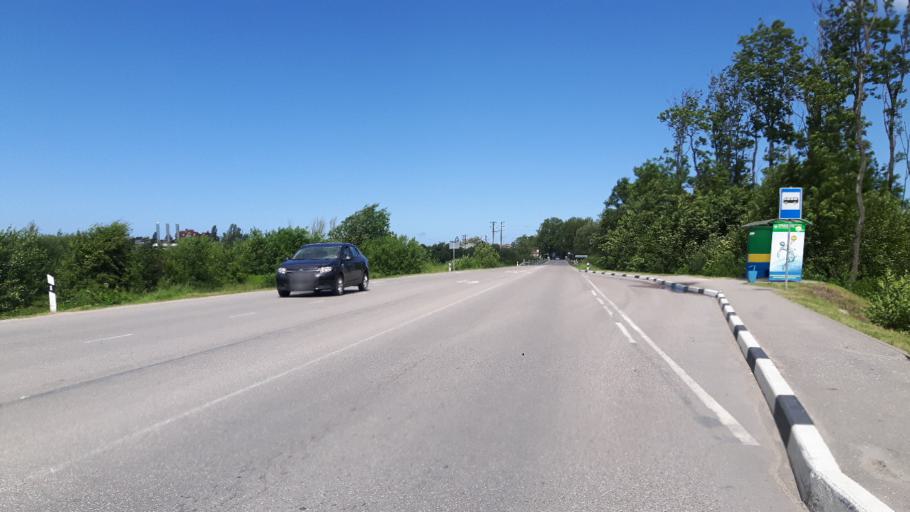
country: RU
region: Kaliningrad
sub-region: Zelenogradskiy Rayon
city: Zelenogradsk
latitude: 54.9458
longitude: 20.4679
